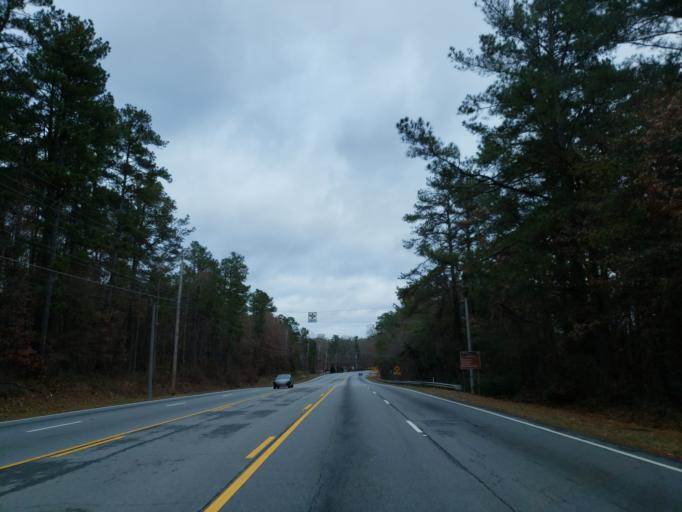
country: US
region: Georgia
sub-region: Cobb County
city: Fair Oaks
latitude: 33.9135
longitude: -84.5928
